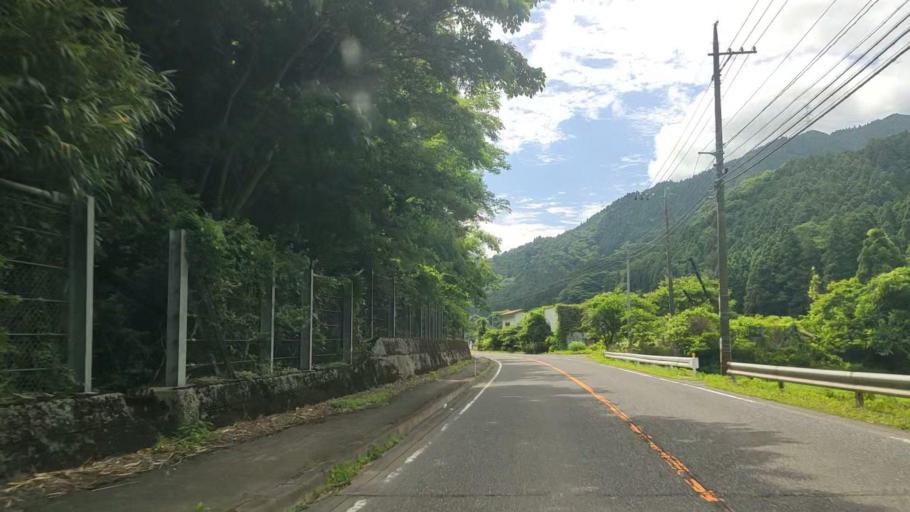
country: JP
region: Okayama
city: Niimi
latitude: 35.2188
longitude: 133.4534
